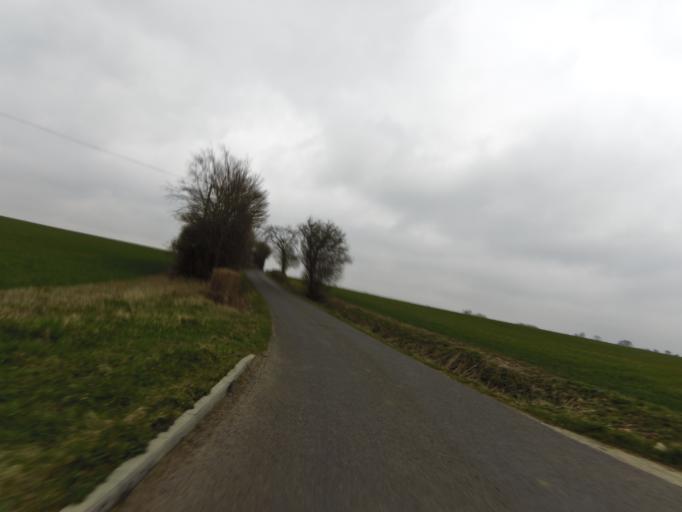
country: GB
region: England
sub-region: Suffolk
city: Framlingham
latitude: 52.2144
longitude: 1.3268
